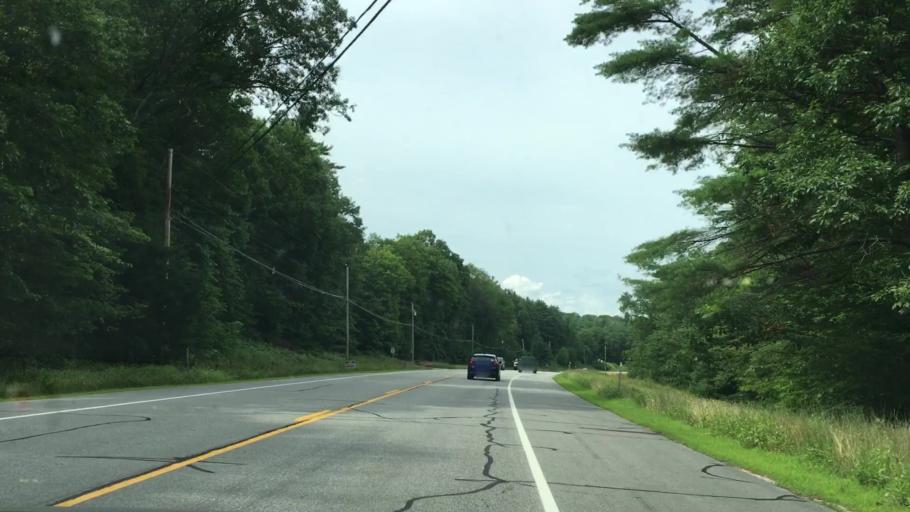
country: US
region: New Hampshire
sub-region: Hillsborough County
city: Hillsborough
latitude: 43.0906
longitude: -71.9199
